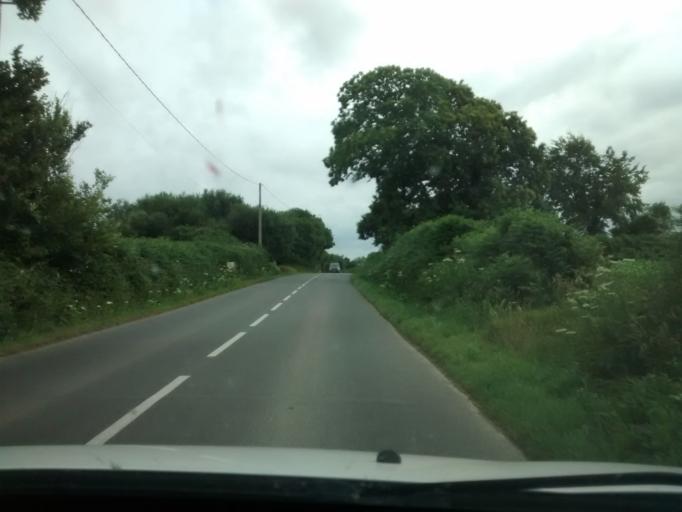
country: FR
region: Brittany
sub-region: Departement des Cotes-d'Armor
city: Plouguiel
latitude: 48.8037
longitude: -3.2371
